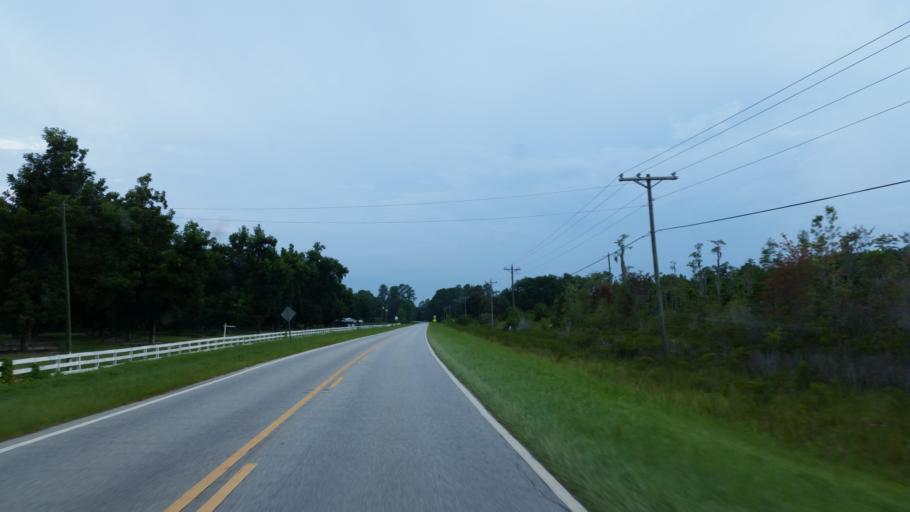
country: US
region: Georgia
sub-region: Lowndes County
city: Valdosta
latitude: 30.7405
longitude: -83.3132
